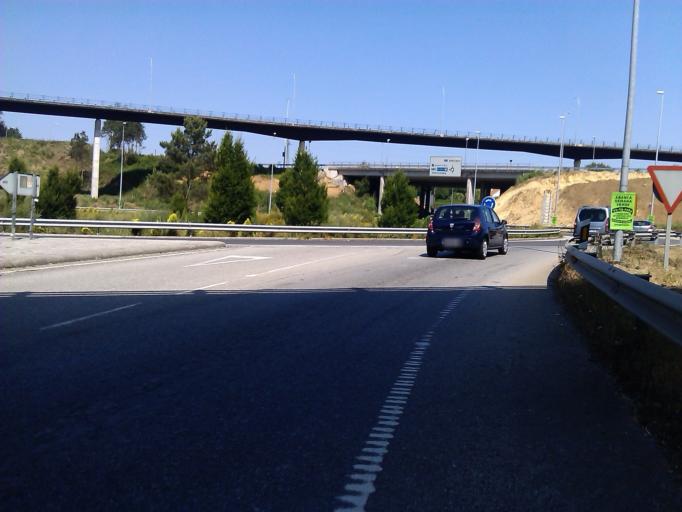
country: ES
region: Galicia
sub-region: Provincia da Coruna
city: Santiago de Compostela
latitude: 42.8550
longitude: -8.5303
